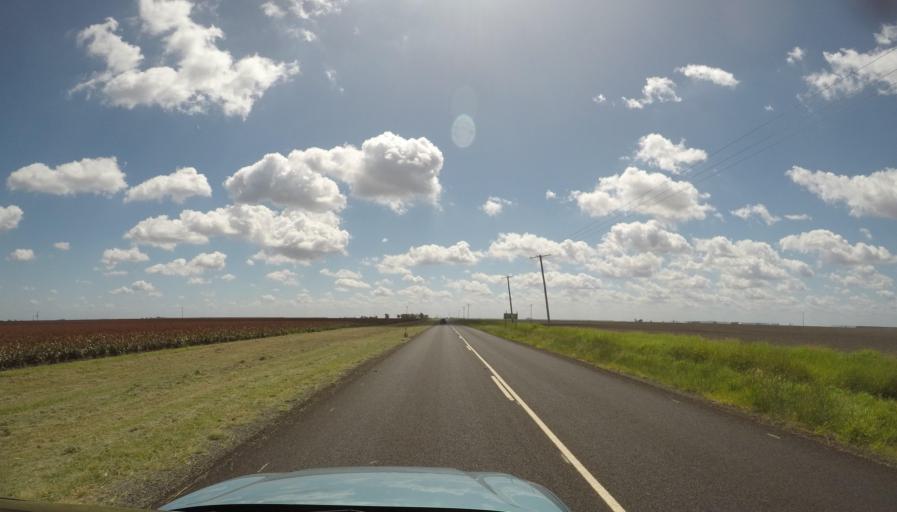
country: AU
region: Queensland
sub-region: Toowoomba
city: Oakey
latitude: -27.5555
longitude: 151.3836
